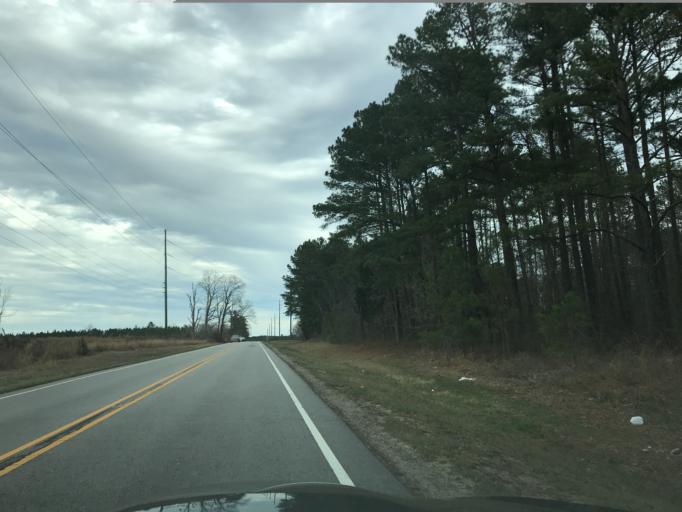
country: US
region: North Carolina
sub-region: Franklin County
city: Louisburg
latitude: 36.0443
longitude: -78.3462
